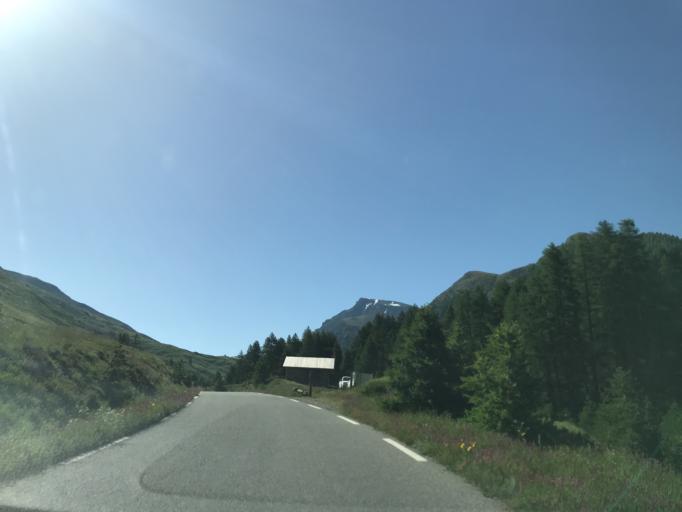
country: IT
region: Piedmont
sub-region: Provincia di Cuneo
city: Pontechianale
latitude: 44.7157
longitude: 6.9141
